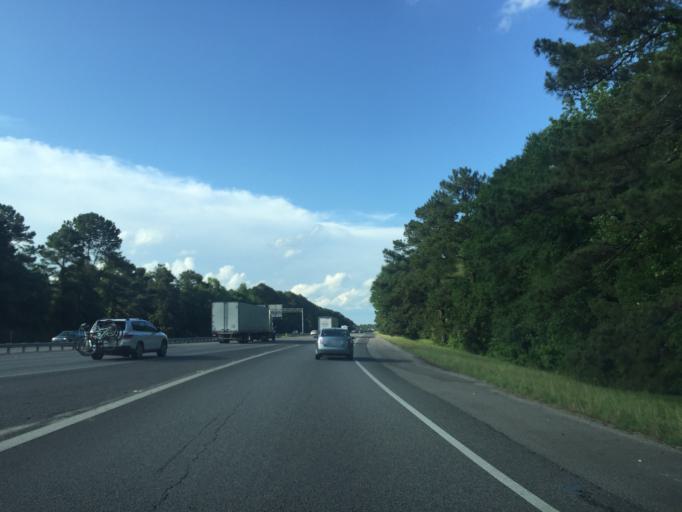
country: US
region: Georgia
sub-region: Chatham County
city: Pooler
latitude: 32.0771
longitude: -81.2442
